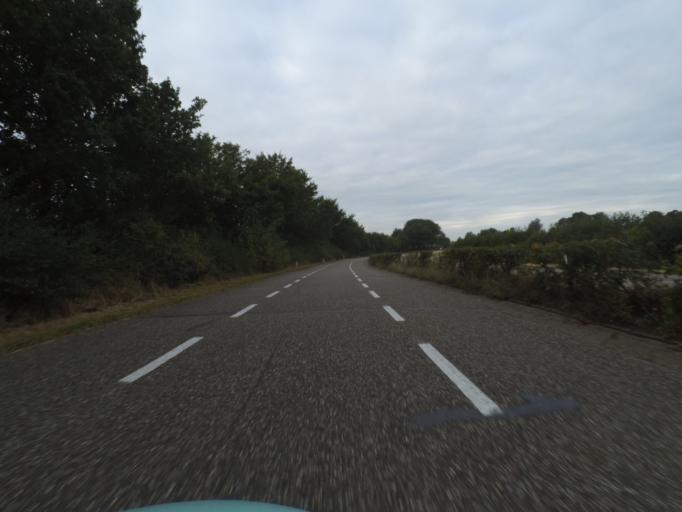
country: NL
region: Utrecht
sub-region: Gemeente Wijk bij Duurstede
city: Wijk bij Duurstede
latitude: 51.9650
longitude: 5.3125
